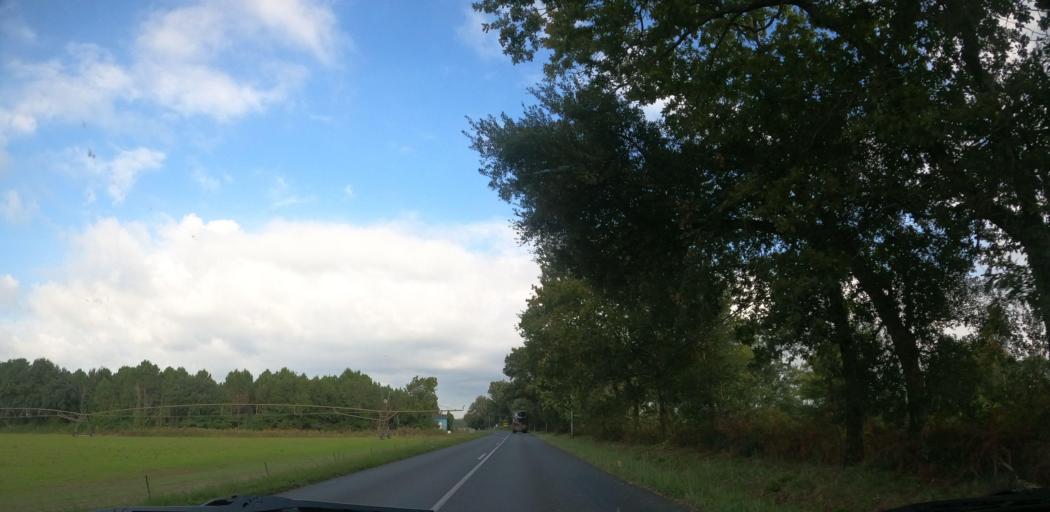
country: FR
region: Aquitaine
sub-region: Departement des Landes
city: Soustons
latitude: 43.7422
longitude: -1.2993
